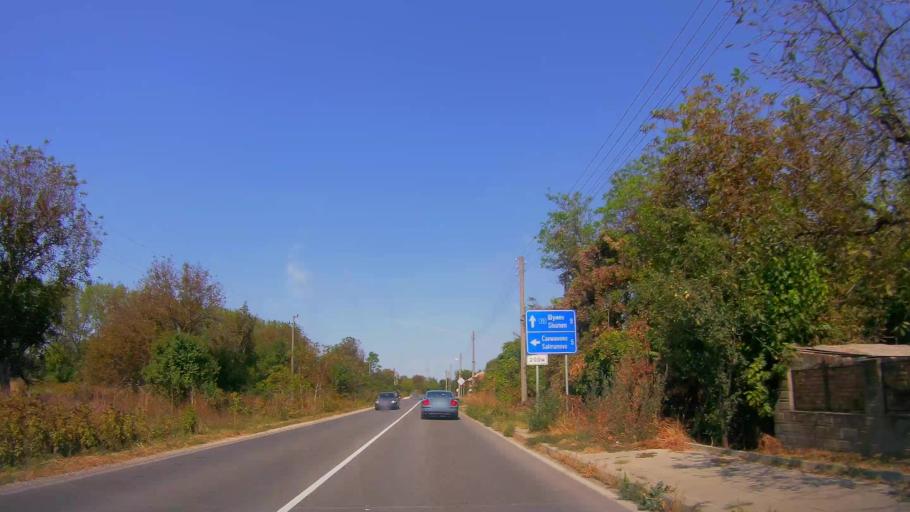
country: BG
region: Shumen
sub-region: Obshtina Smyadovo
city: Smyadovo
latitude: 43.1796
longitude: 27.0071
